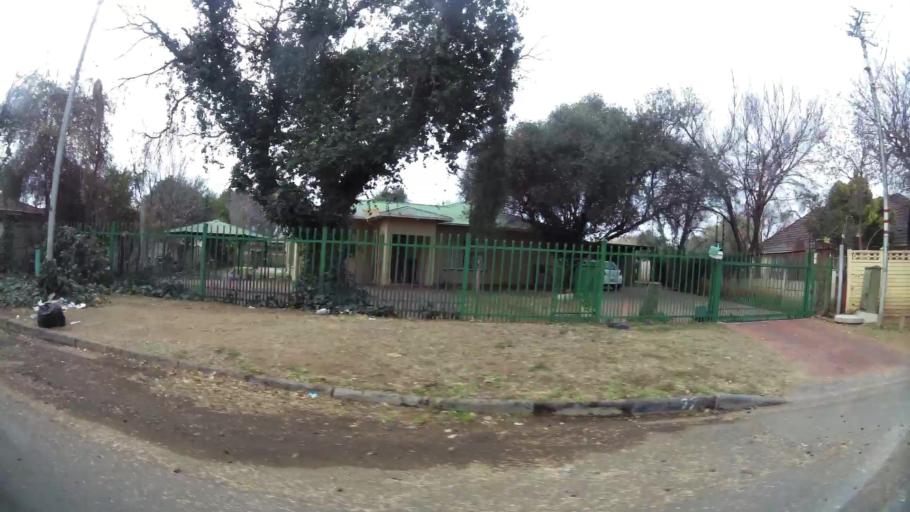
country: ZA
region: Orange Free State
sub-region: Mangaung Metropolitan Municipality
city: Bloemfontein
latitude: -29.1237
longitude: 26.1961
